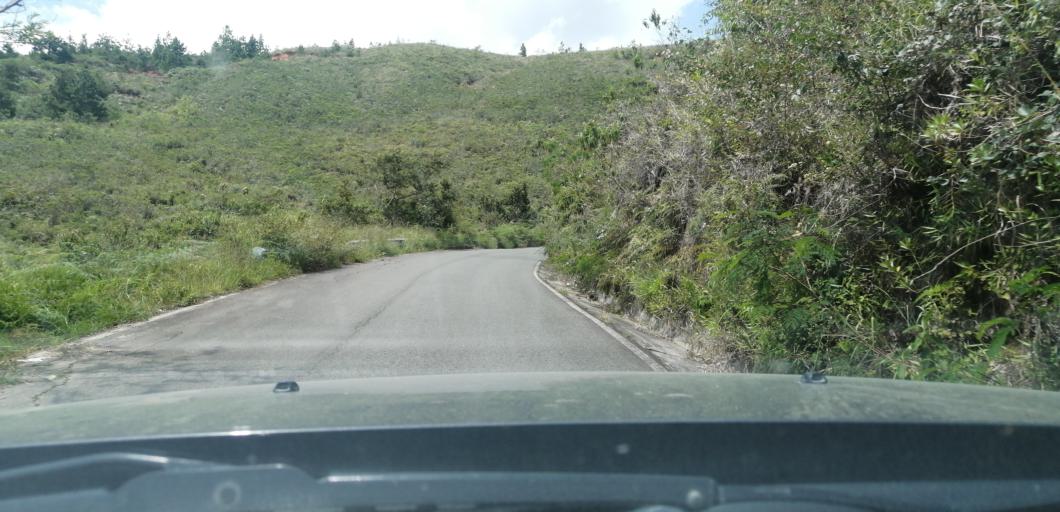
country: CO
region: Valle del Cauca
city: Dagua
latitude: 3.7118
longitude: -76.5836
